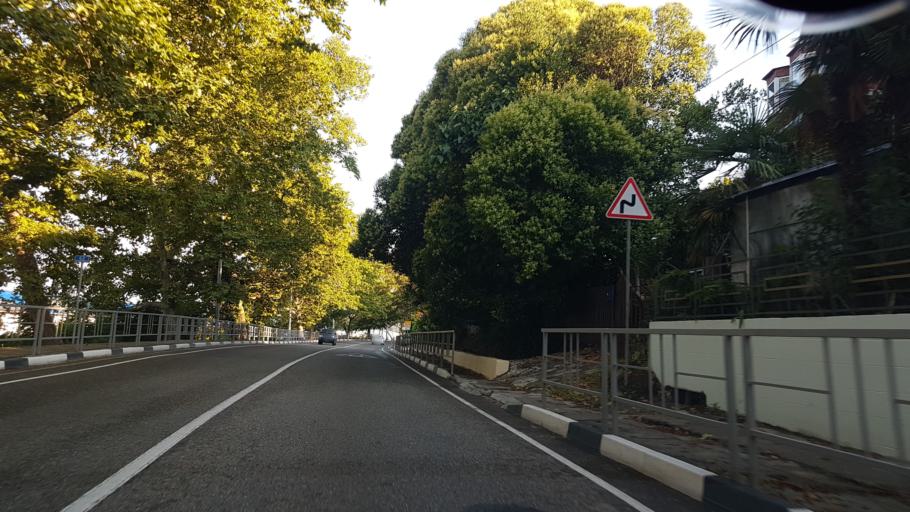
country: RU
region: Krasnodarskiy
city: Gornoye Loo
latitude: 43.6920
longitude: 39.5924
